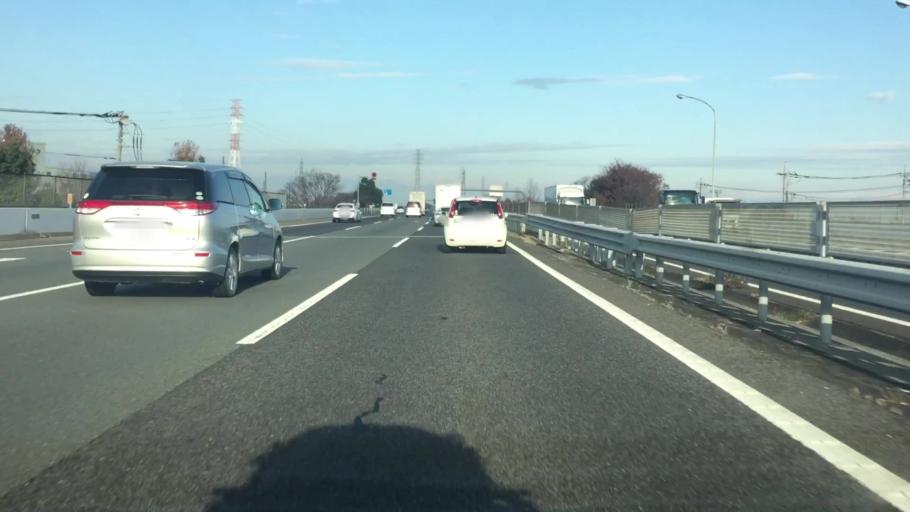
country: JP
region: Saitama
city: Honjo
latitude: 36.2202
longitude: 139.1632
